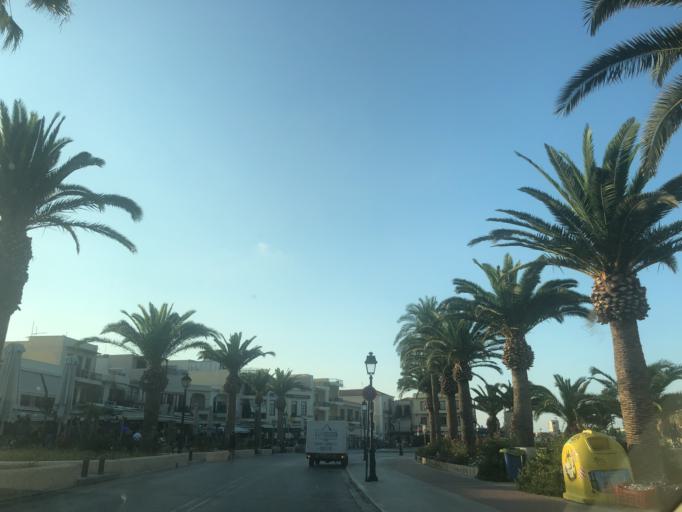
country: GR
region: Crete
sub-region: Nomos Rethymnis
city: Rethymno
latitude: 35.3687
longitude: 24.4769
